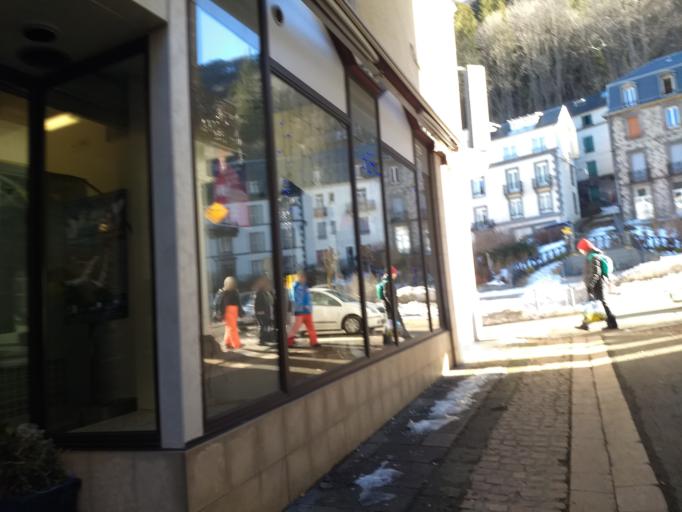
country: FR
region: Auvergne
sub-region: Departement du Puy-de-Dome
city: Mont-Dore
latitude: 45.5734
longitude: 2.8108
